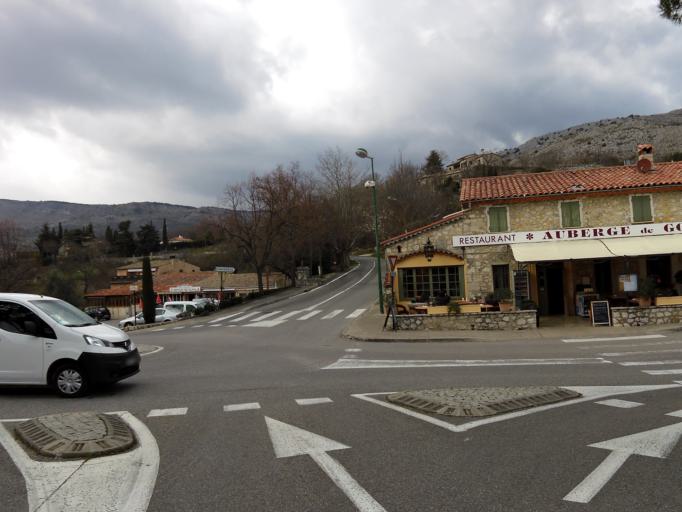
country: FR
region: Provence-Alpes-Cote d'Azur
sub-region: Departement des Alpes-Maritimes
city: Opio
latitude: 43.7213
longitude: 6.9772
